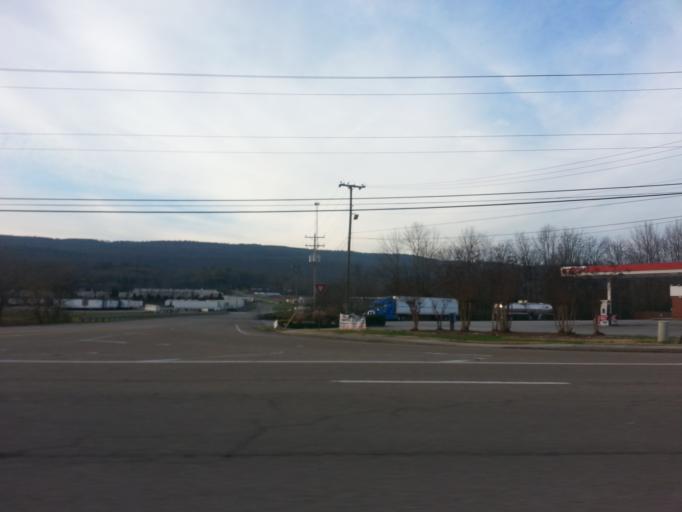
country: US
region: Tennessee
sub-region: Rhea County
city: Dayton
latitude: 35.5266
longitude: -84.9878
